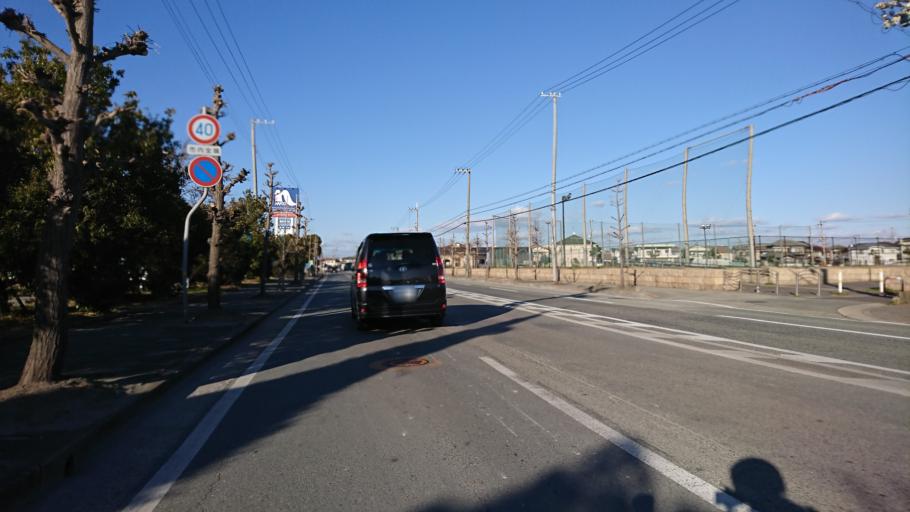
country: JP
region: Hyogo
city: Kakogawacho-honmachi
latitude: 34.7356
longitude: 134.8219
